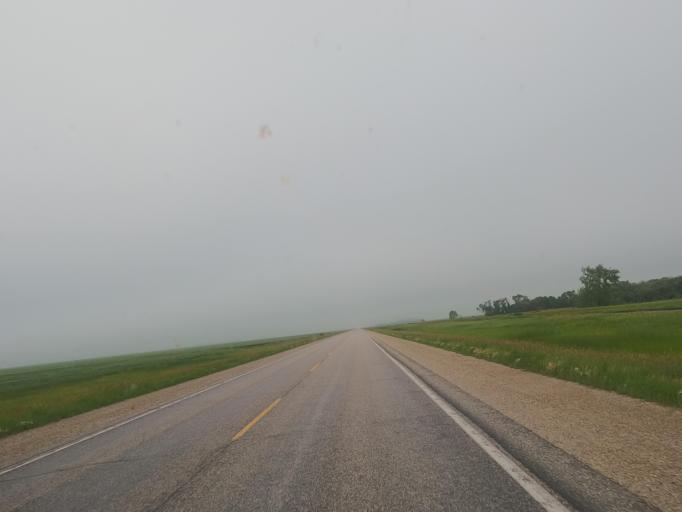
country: CA
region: Manitoba
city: Carman
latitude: 49.7254
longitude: -97.8750
